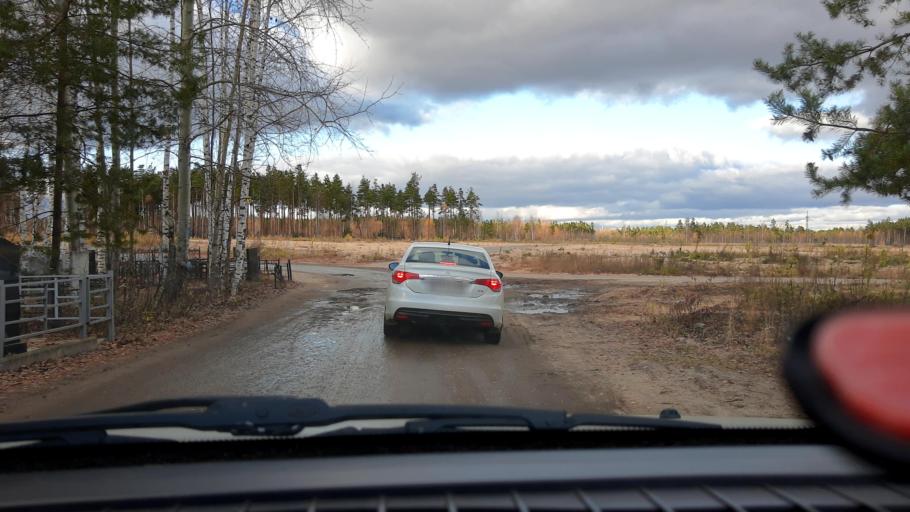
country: RU
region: Nizjnij Novgorod
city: Gorbatovka
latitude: 56.3598
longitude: 43.7733
